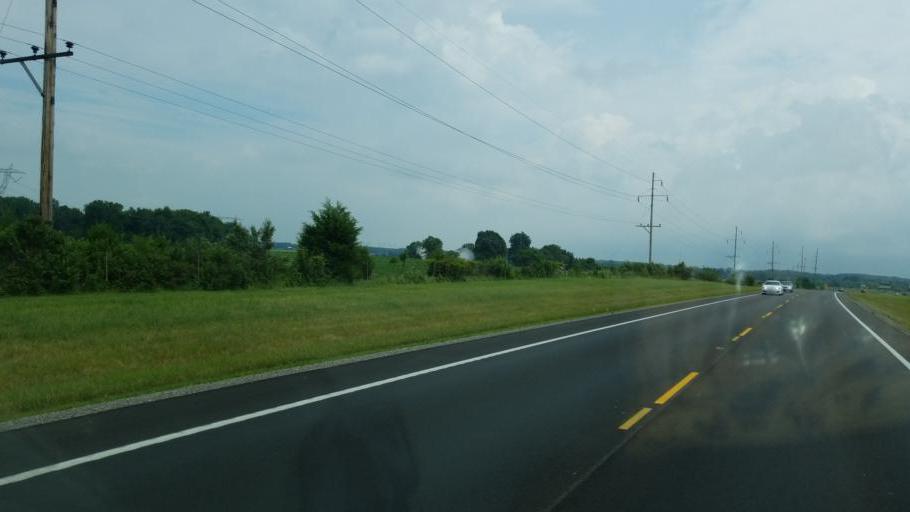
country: US
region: Ohio
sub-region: Logan County
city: Russells Point
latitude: 40.4488
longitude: -83.8267
